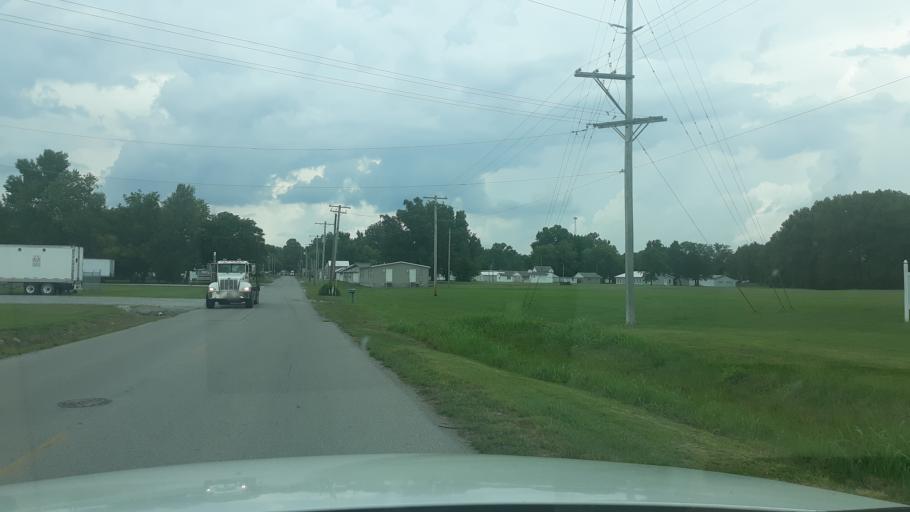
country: US
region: Illinois
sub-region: Saline County
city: Eldorado
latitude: 37.8030
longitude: -88.4566
